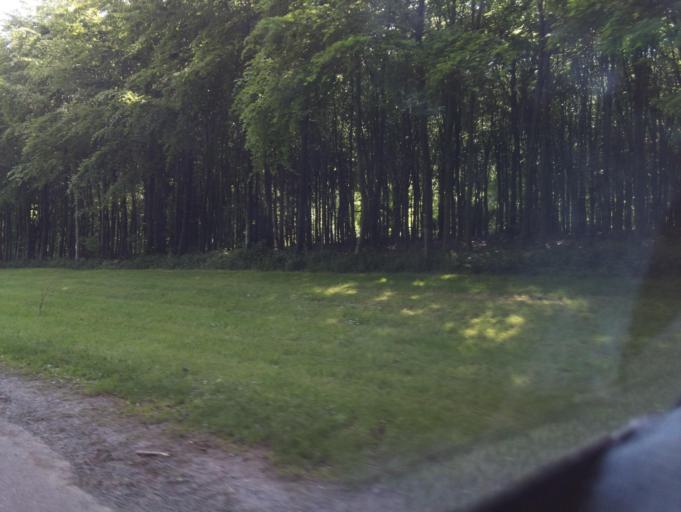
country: GB
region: England
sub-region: Wiltshire
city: Luckington
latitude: 51.5736
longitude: -2.2741
